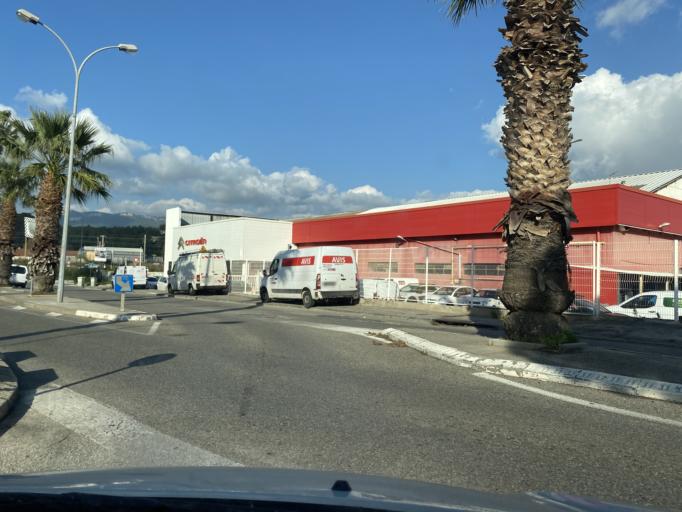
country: FR
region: Provence-Alpes-Cote d'Azur
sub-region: Departement du Var
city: La Seyne-sur-Mer
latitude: 43.1142
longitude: 5.8723
